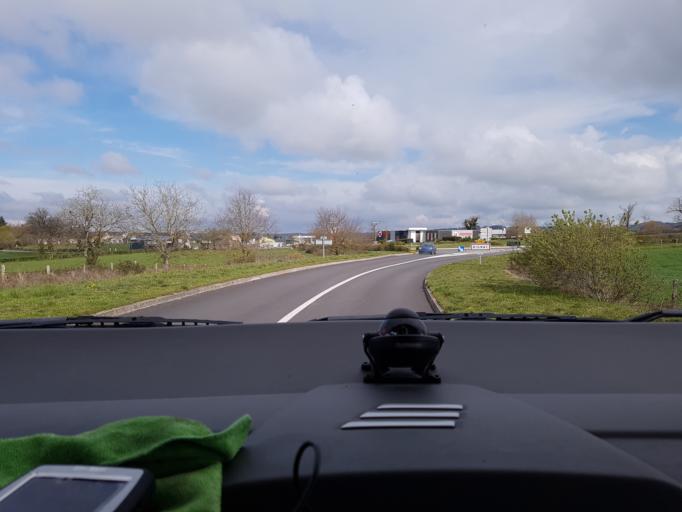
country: FR
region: Midi-Pyrenees
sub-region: Departement de l'Aveyron
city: Colombies
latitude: 44.4011
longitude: 2.3003
